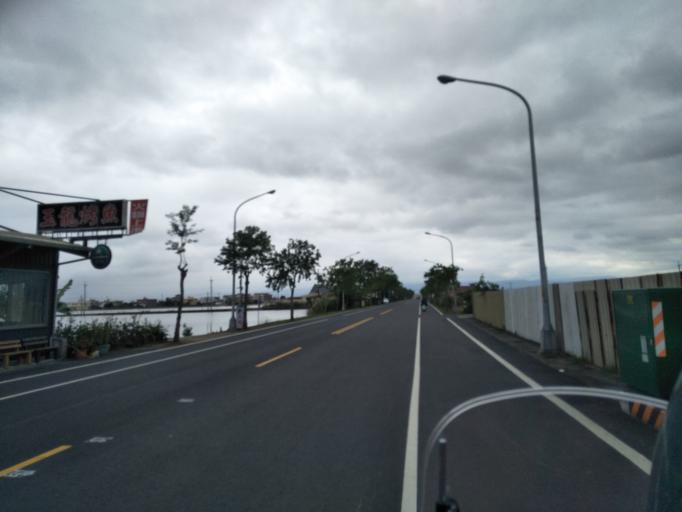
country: TW
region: Taiwan
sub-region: Yilan
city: Yilan
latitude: 24.8156
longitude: 121.7947
